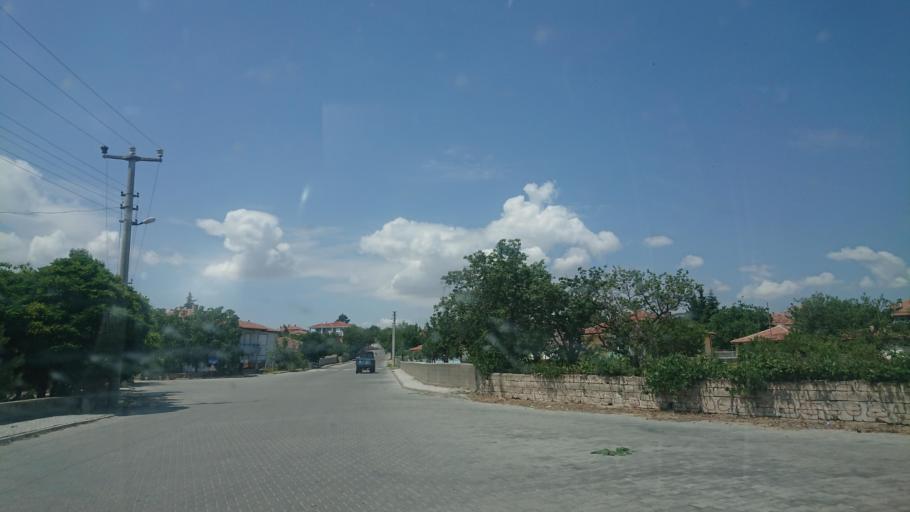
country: TR
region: Aksaray
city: Sariyahsi
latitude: 38.9787
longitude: 33.8405
